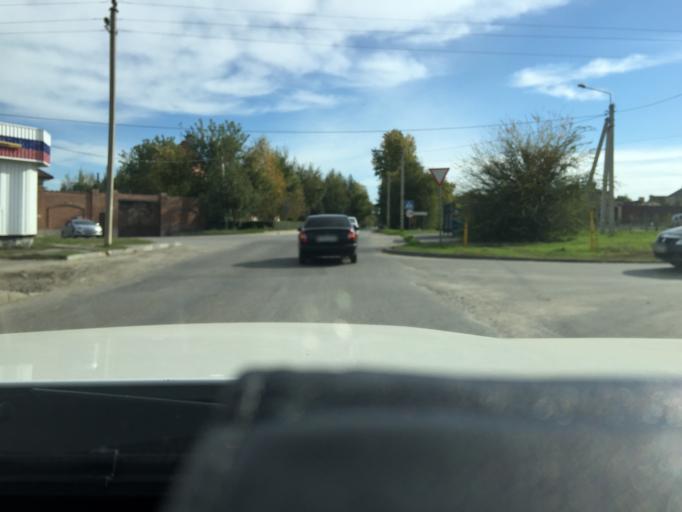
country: RU
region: Rostov
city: Aksay
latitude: 47.3018
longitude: 39.8198
